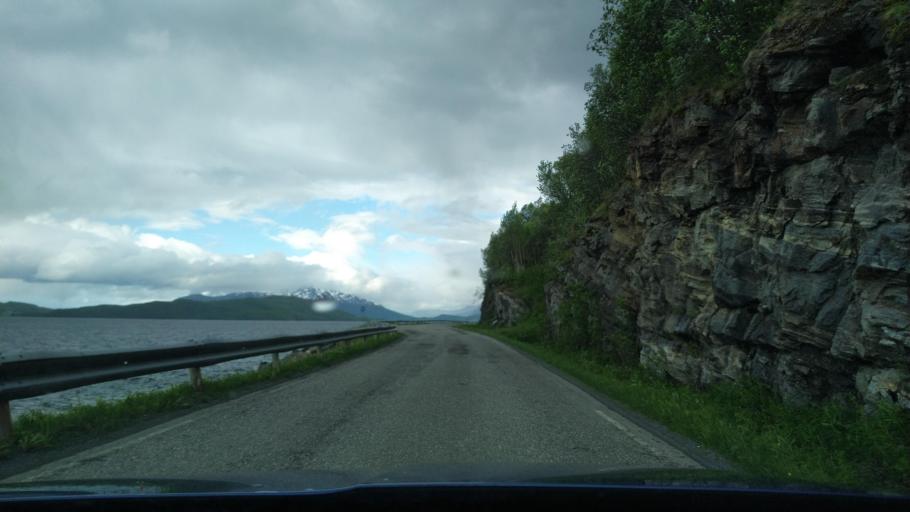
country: NO
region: Troms
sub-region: Lenvik
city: Finnsnes
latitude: 69.1396
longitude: 17.9094
